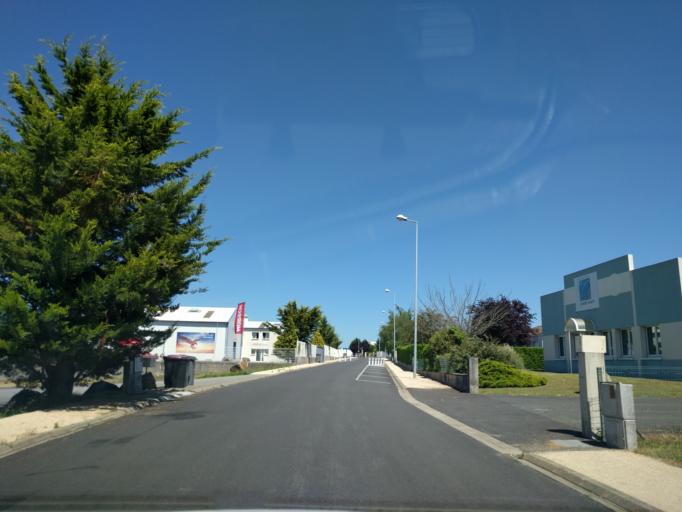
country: FR
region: Poitou-Charentes
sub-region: Departement des Deux-Sevres
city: Aiffres
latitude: 46.3292
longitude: -0.4123
